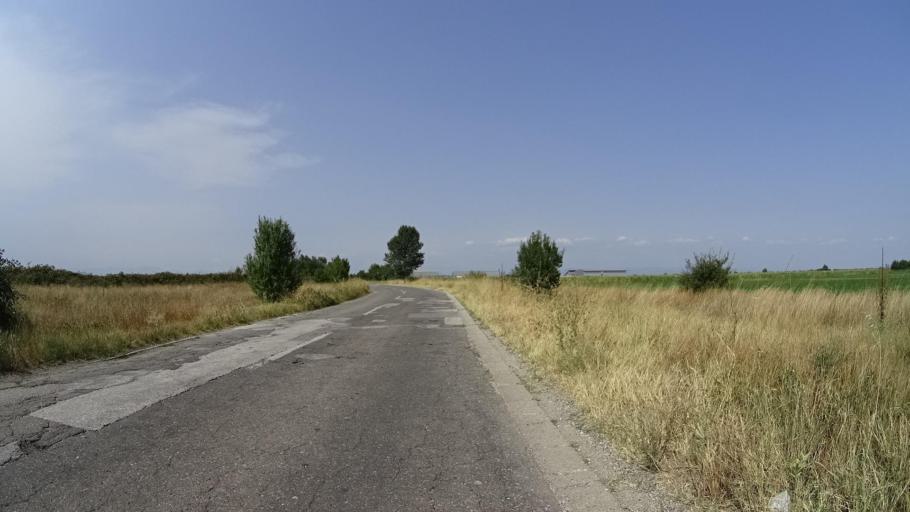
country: BG
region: Plovdiv
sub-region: Obshtina Plovdiv
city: Plovdiv
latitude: 42.2265
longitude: 24.7861
